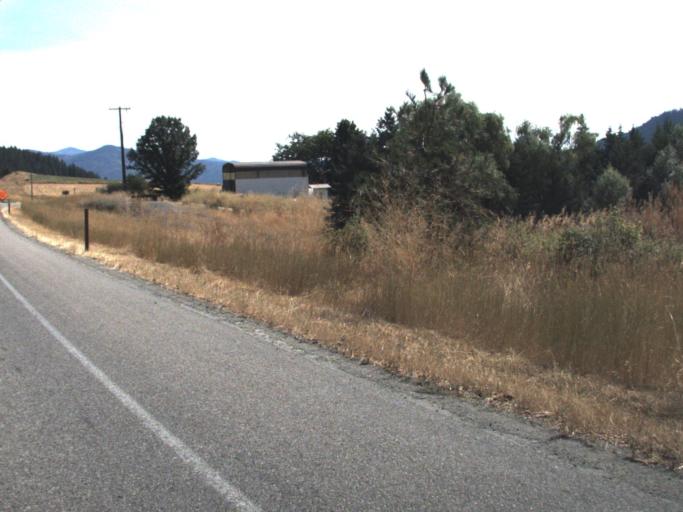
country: US
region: Washington
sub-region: Stevens County
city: Chewelah
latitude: 48.3113
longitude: -117.7923
